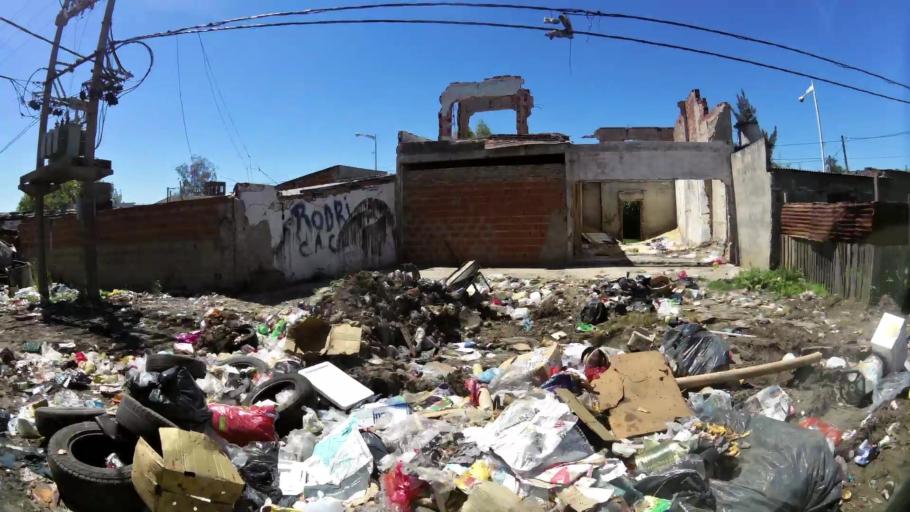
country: AR
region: Santa Fe
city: Santa Fe de la Vera Cruz
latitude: -31.6326
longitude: -60.7252
